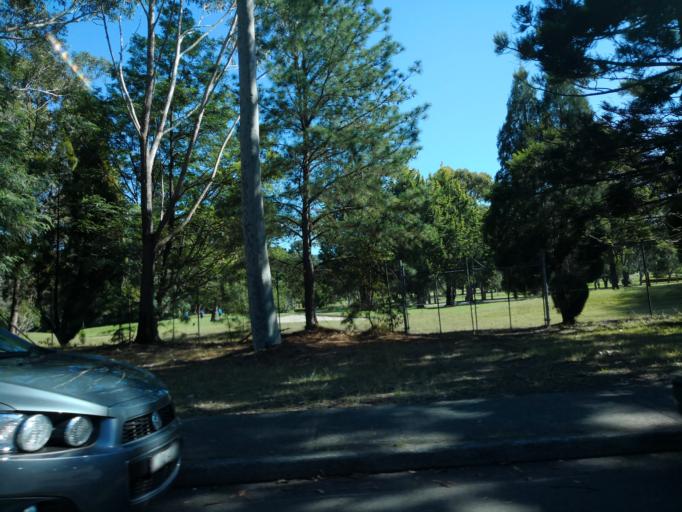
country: AU
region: New South Wales
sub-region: Gosford Shire
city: Gosford
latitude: -33.4198
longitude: 151.3371
